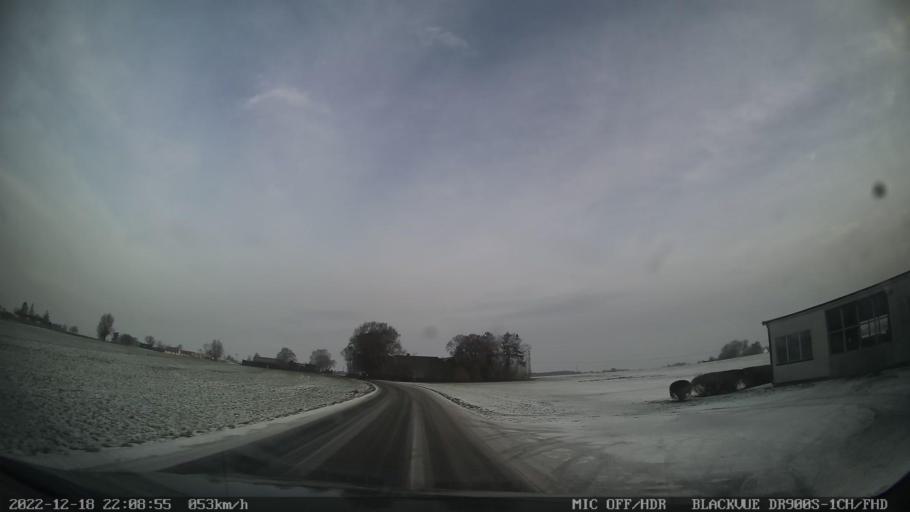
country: SE
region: Skane
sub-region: Tomelilla Kommun
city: Tomelilla
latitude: 55.5289
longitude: 14.0419
